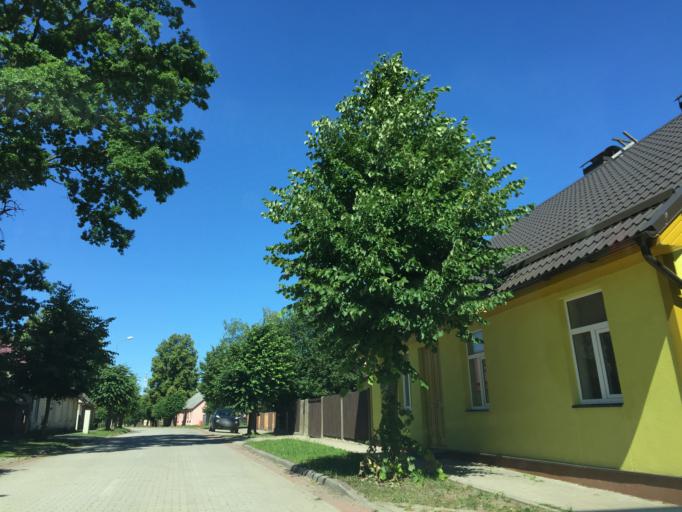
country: LV
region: Ventspils Rajons
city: Piltene
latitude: 57.2274
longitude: 21.6741
